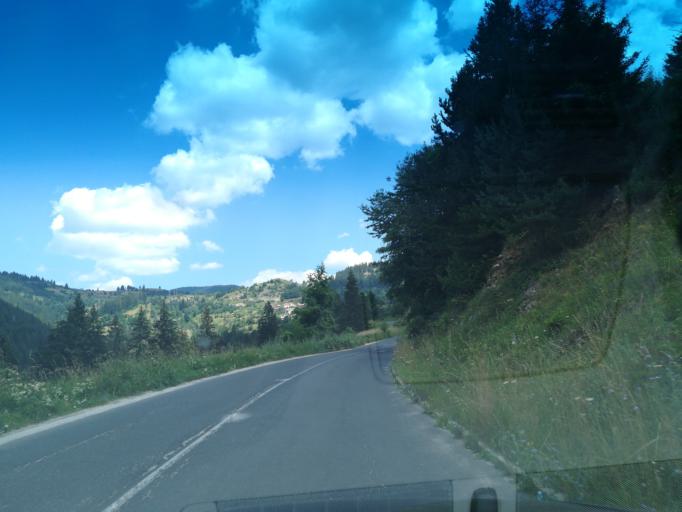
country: BG
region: Smolyan
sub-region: Obshtina Smolyan
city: Smolyan
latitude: 41.6583
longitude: 24.7680
